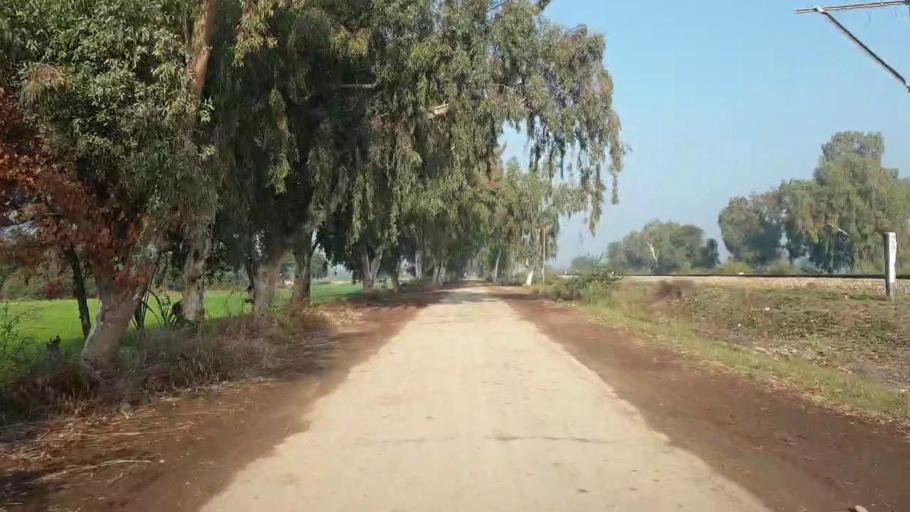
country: PK
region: Sindh
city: Shahdadpur
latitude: 25.9656
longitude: 68.6110
